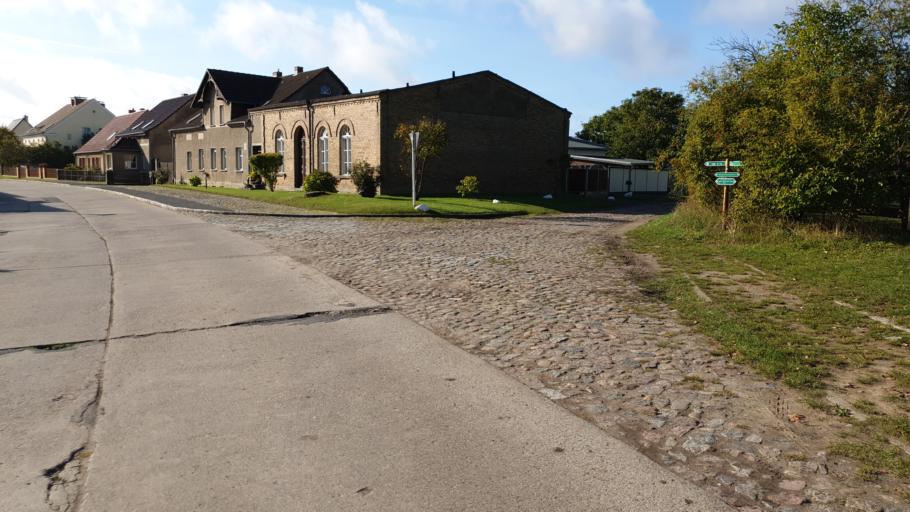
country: DE
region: Brandenburg
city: Liepe
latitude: 52.9093
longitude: 13.9595
